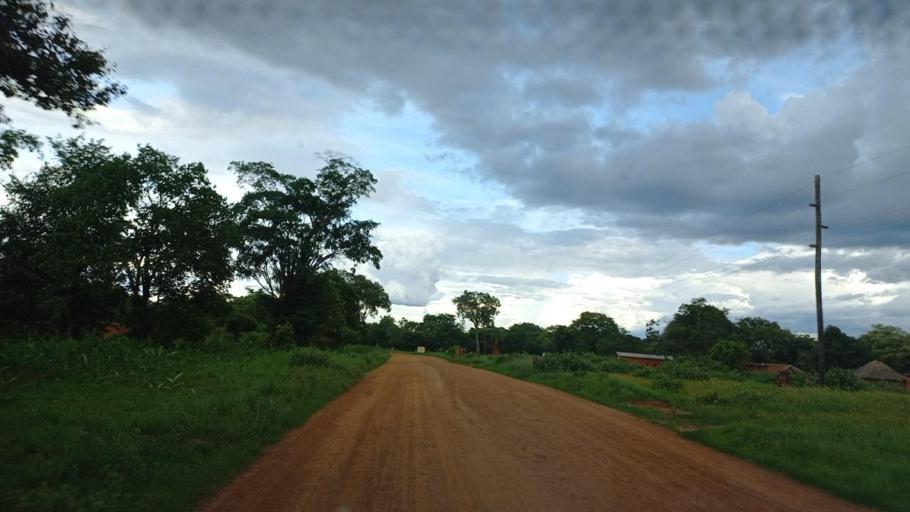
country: ZM
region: North-Western
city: Mwinilunga
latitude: -11.7742
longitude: 24.4027
